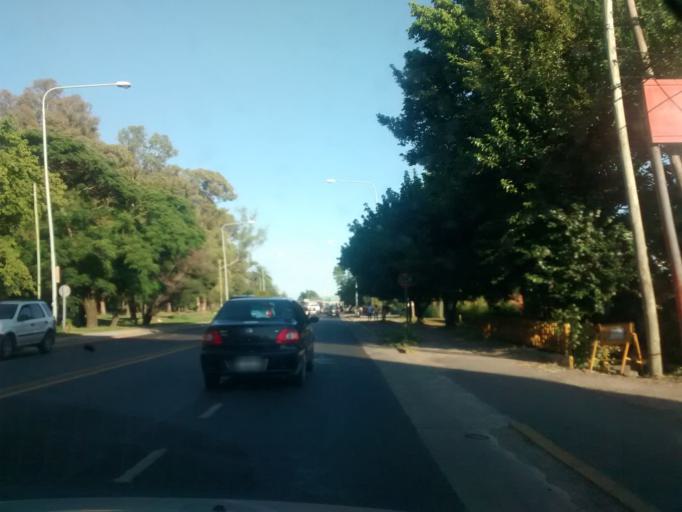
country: AR
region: Buenos Aires
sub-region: Partido de La Plata
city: La Plata
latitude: -34.9043
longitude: -57.9309
